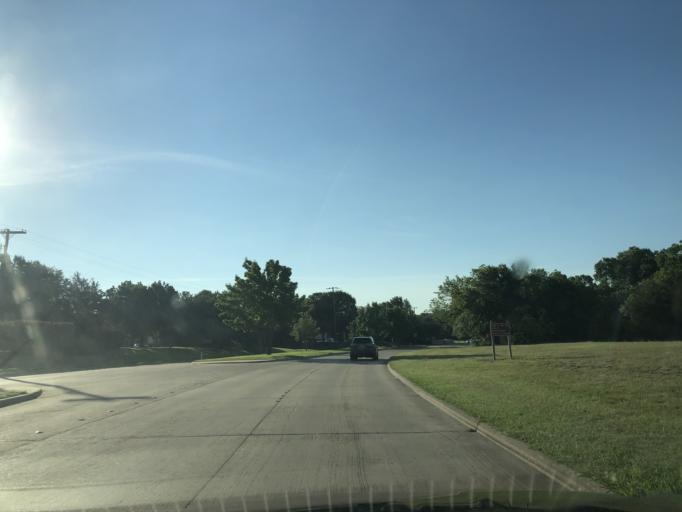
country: US
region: Texas
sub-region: Dallas County
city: Sunnyvale
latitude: 32.8481
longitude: -96.6048
